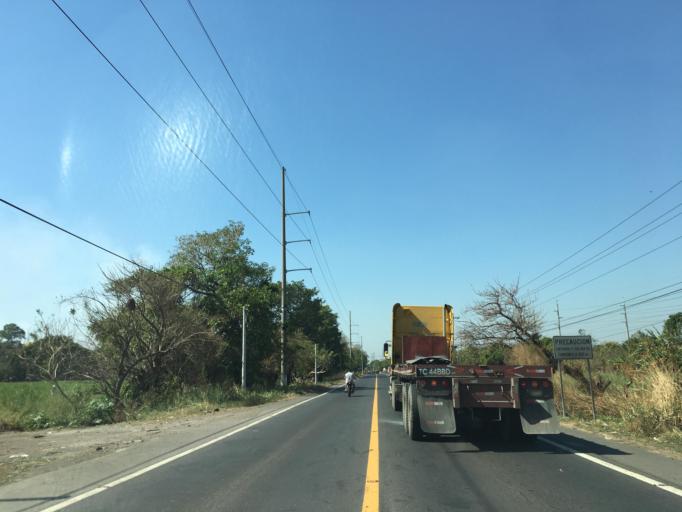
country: GT
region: Escuintla
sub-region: Municipio de Masagua
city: Masagua
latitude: 14.2395
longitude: -90.8170
